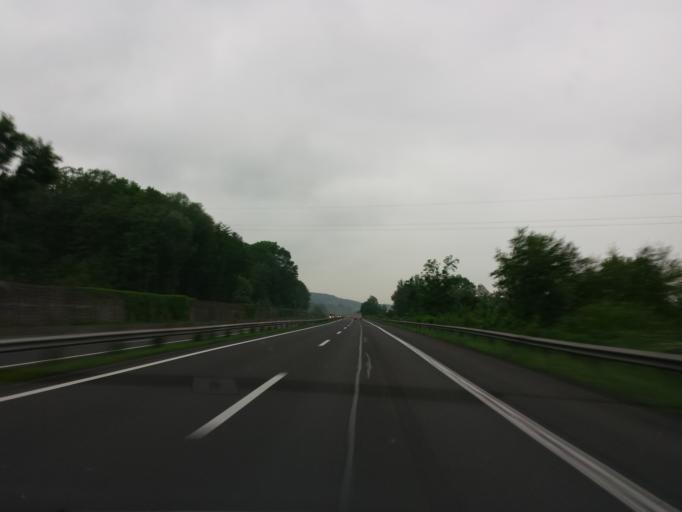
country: AT
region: Styria
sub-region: Politischer Bezirk Hartberg-Fuerstenfeld
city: Ilz
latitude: 47.0802
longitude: 15.9158
